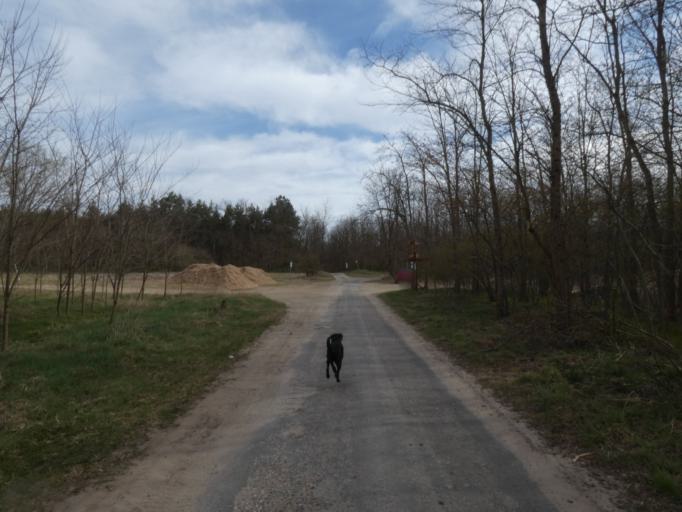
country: HU
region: Pest
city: Kakucs
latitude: 47.2722
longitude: 19.3567
